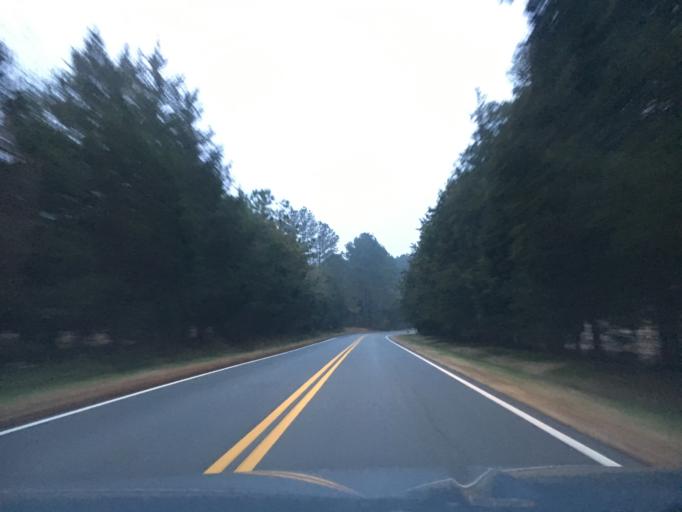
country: US
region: Virginia
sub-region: Halifax County
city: South Boston
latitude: 36.6999
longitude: -78.9630
